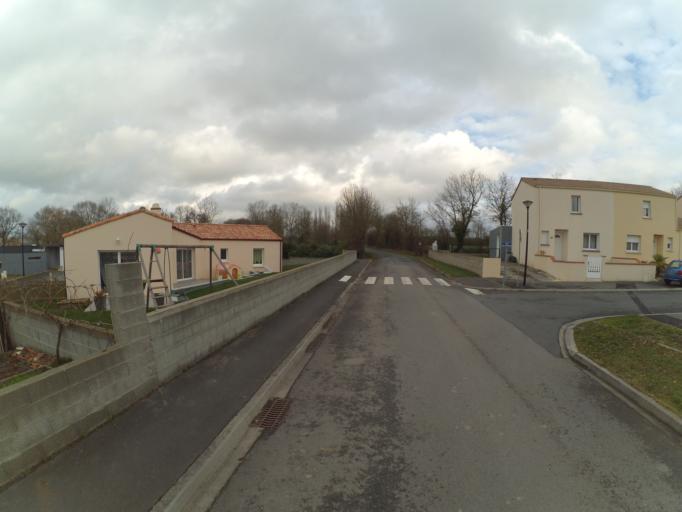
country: FR
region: Pays de la Loire
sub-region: Departement de la Vendee
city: Saint-Hilaire-de-Loulay
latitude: 47.0056
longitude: -1.3225
